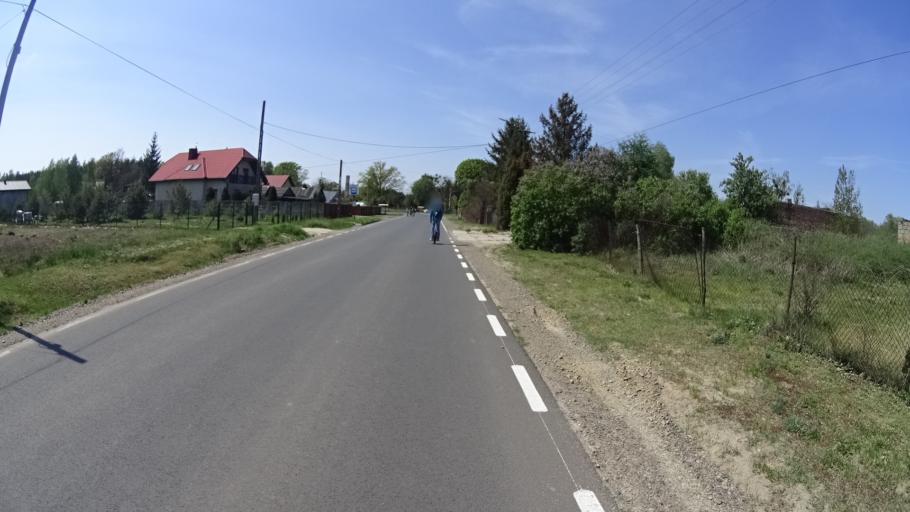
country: PL
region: Masovian Voivodeship
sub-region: Powiat warszawski zachodni
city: Truskaw
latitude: 52.2790
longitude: 20.7146
